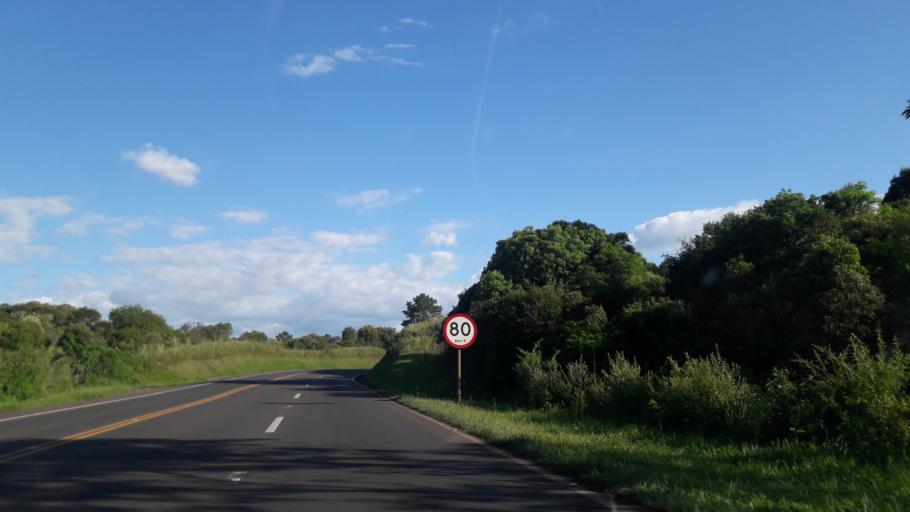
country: BR
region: Parana
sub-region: Guarapuava
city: Guarapuava
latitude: -25.3620
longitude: -51.3507
